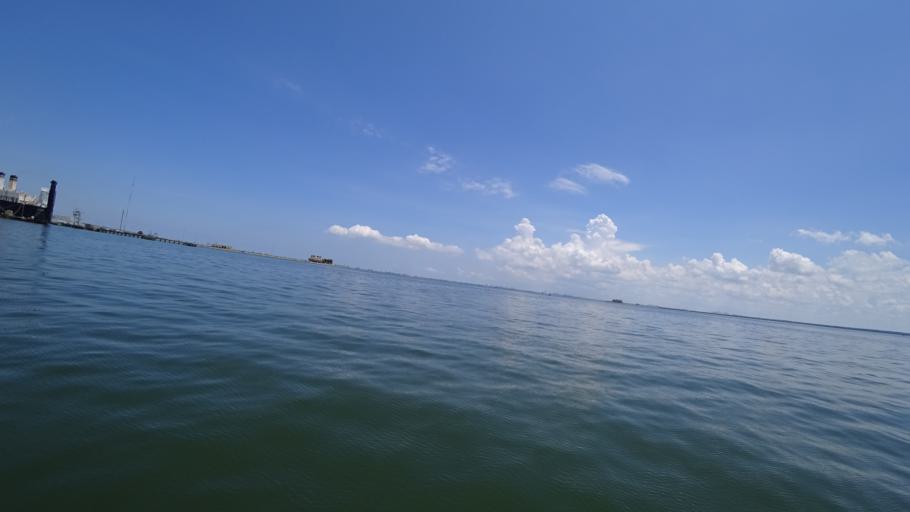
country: US
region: Virginia
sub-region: City of Newport News
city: Newport News
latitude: 36.9588
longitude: -76.4210
